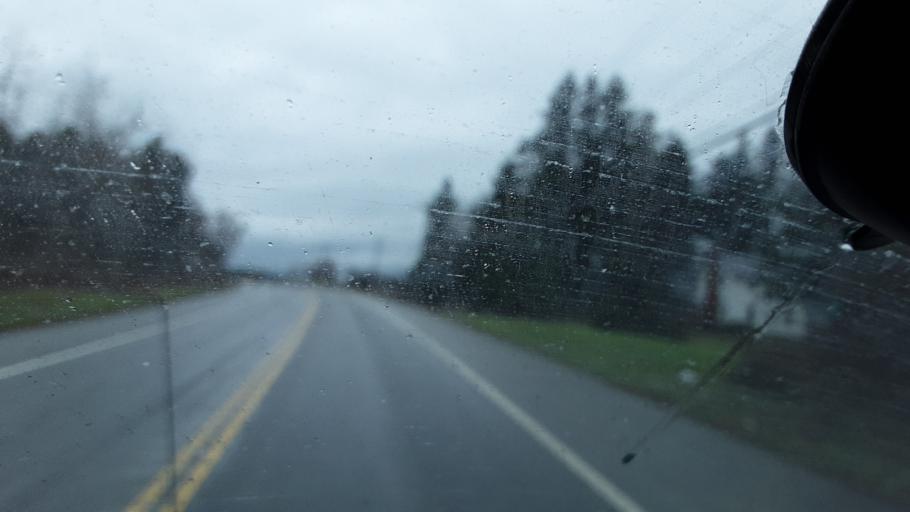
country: US
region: New York
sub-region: Cattaraugus County
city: Yorkshire
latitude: 42.5854
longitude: -78.4907
